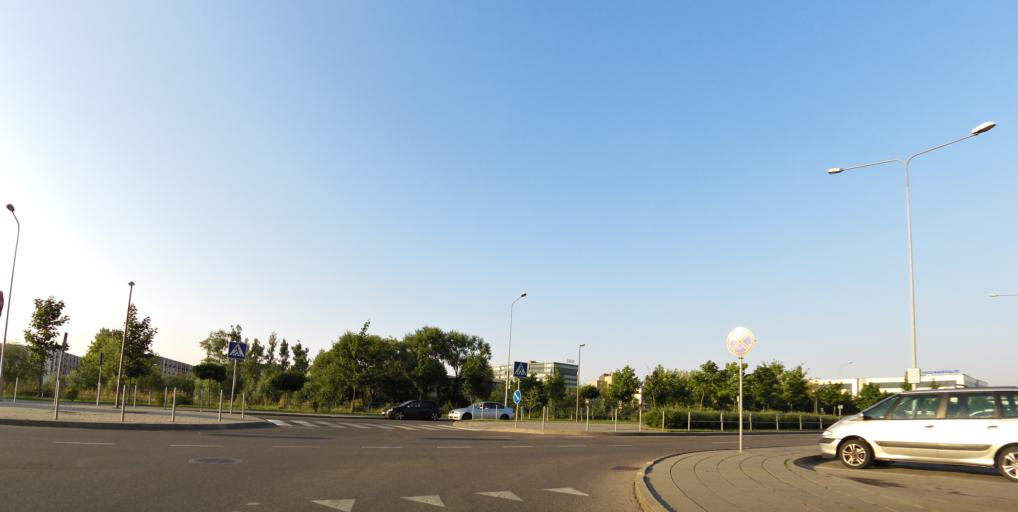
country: LT
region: Vilnius County
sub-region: Vilnius
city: Vilnius
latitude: 54.7169
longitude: 25.2819
